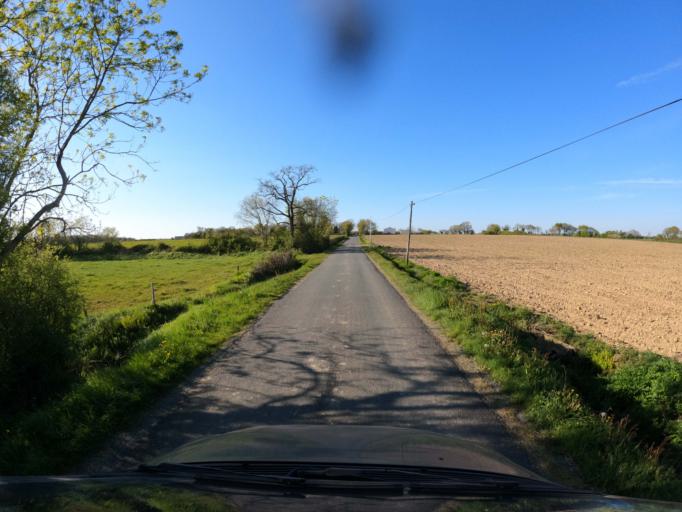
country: FR
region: Pays de la Loire
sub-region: Departement de la Vendee
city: Les Brouzils
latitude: 46.8934
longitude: -1.3677
